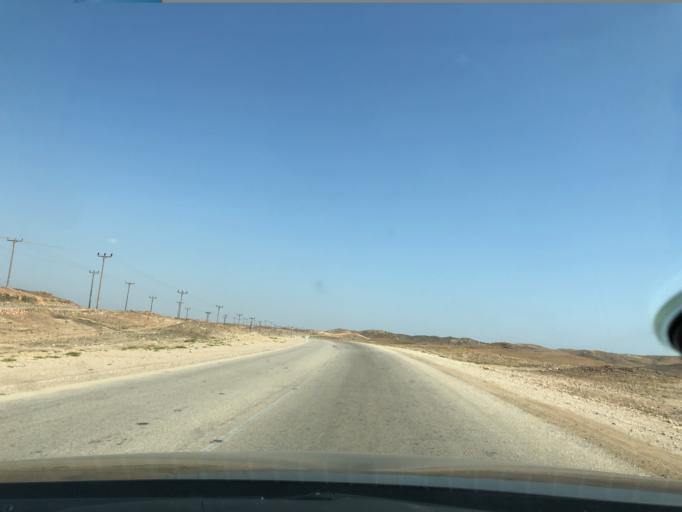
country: OM
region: Zufar
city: Salalah
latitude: 17.0010
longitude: 54.7378
